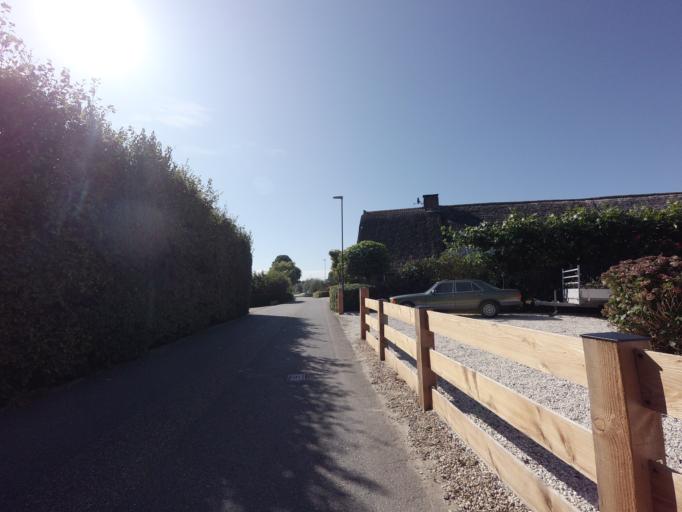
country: NL
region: South Holland
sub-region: Gemeente Giessenlanden
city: Giessenburg
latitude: 51.8817
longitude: 4.9264
